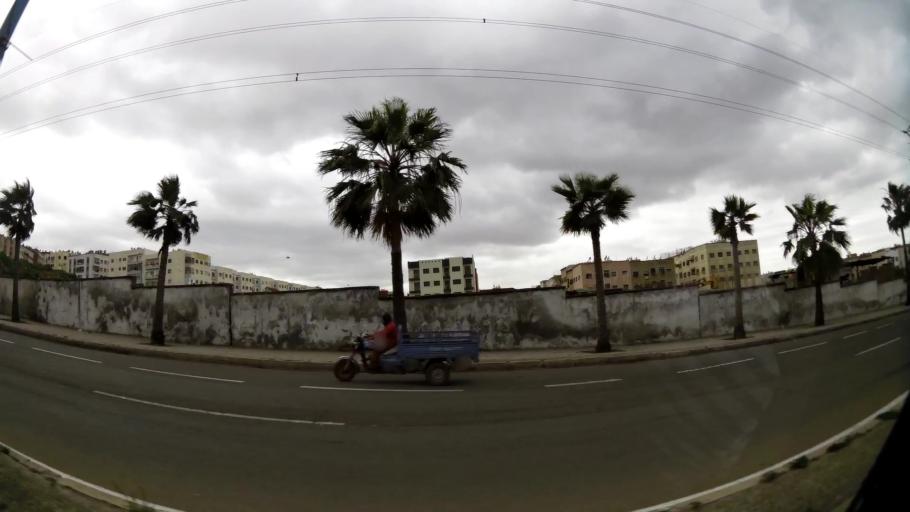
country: MA
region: Grand Casablanca
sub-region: Mediouna
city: Tit Mellil
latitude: 33.5726
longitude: -7.5364
